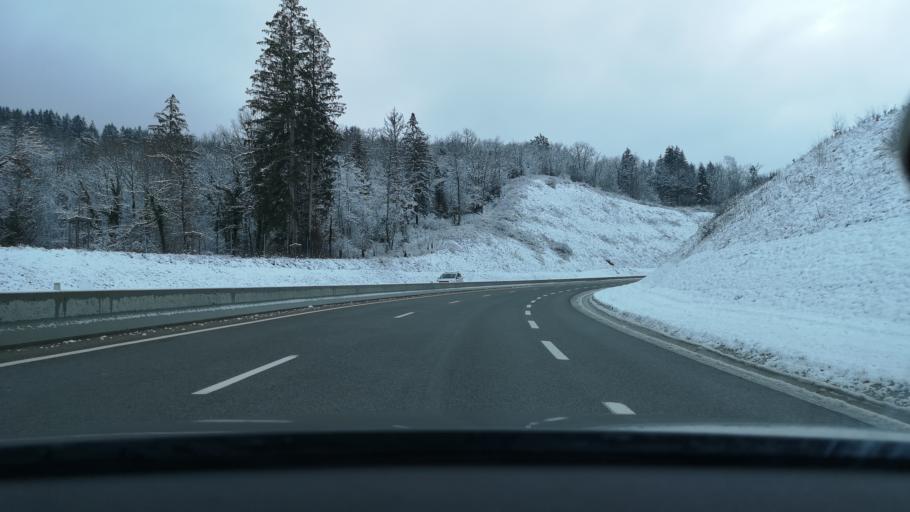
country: FR
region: Rhone-Alpes
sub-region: Departement de l'Ain
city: Dortan
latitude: 46.3222
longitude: 5.6743
